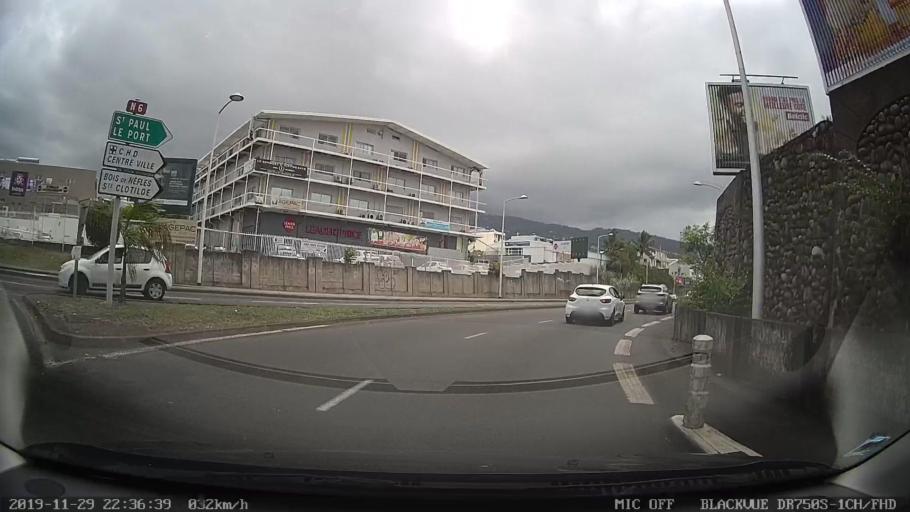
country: RE
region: Reunion
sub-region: Reunion
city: Saint-Denis
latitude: -20.9006
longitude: 55.4923
